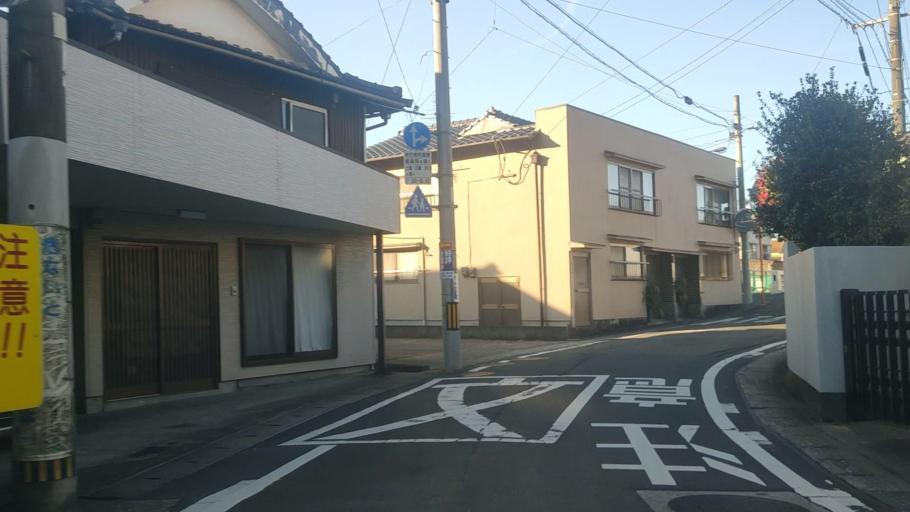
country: JP
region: Oita
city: Beppu
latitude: 33.2698
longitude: 131.5061
